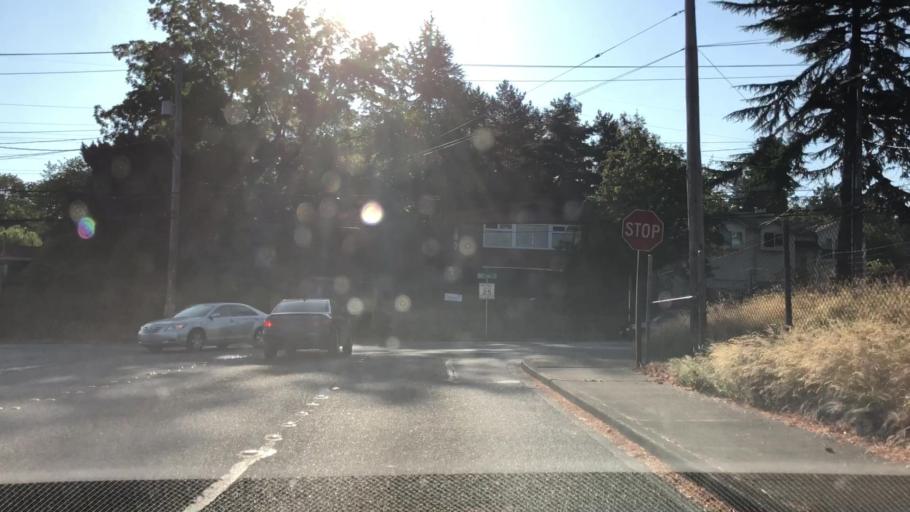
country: US
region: Washington
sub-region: King County
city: Bryn Mawr-Skyway
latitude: 47.5095
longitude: -122.2705
